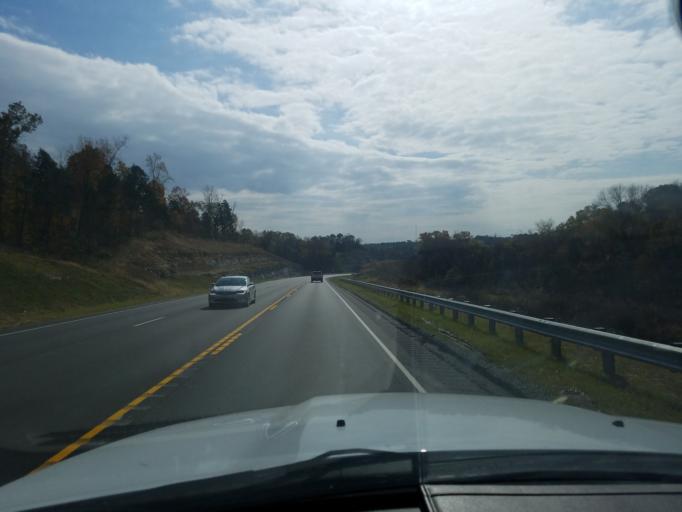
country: US
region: Kentucky
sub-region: Bullitt County
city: Mount Washington
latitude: 37.9956
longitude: -85.4935
